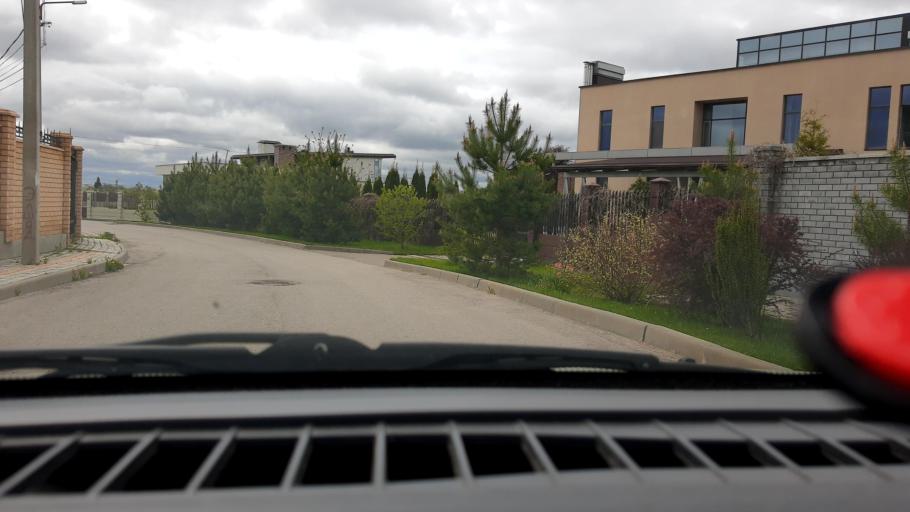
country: RU
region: Nizjnij Novgorod
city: Afonino
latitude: 56.2805
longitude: 44.0705
